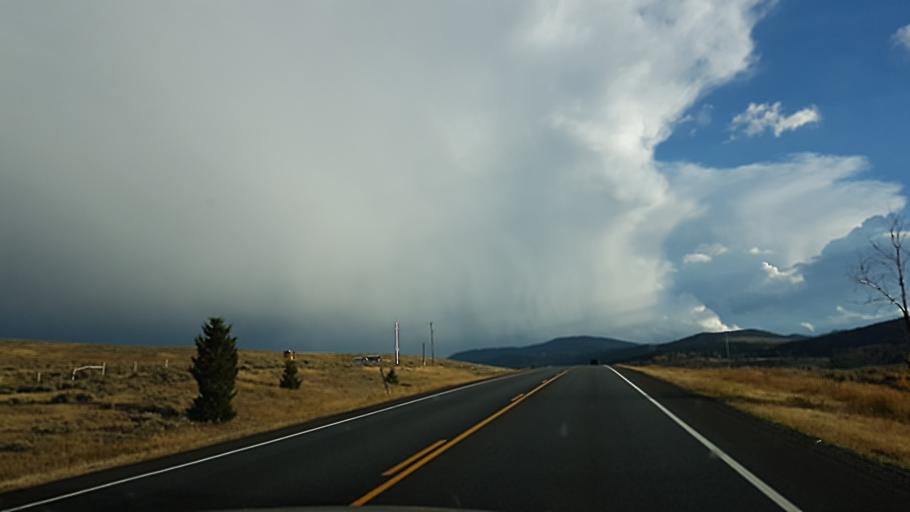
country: US
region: Montana
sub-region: Gallatin County
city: West Yellowstone
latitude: 44.7297
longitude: -111.4703
